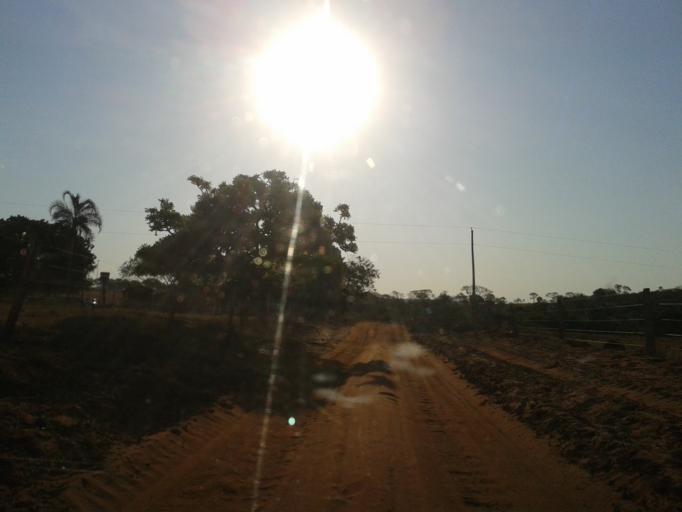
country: BR
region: Minas Gerais
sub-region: Ituiutaba
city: Ituiutaba
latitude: -19.2485
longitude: -49.5796
